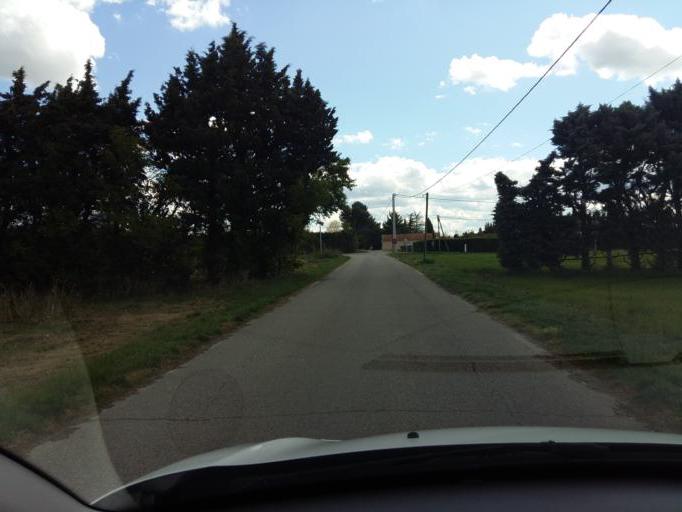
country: FR
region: Provence-Alpes-Cote d'Azur
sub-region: Departement du Vaucluse
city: Le Thor
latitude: 43.9298
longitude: 5.0192
